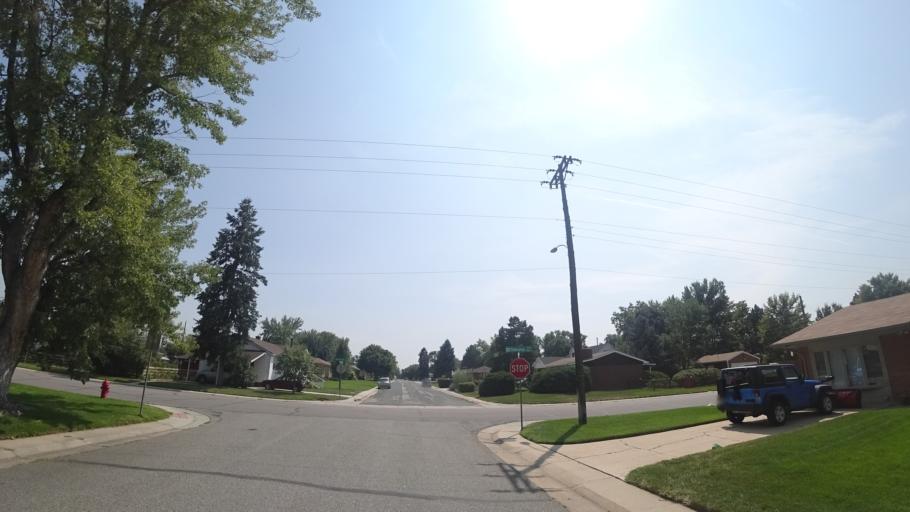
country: US
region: Colorado
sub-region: Arapahoe County
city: Englewood
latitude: 39.6279
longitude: -104.9938
